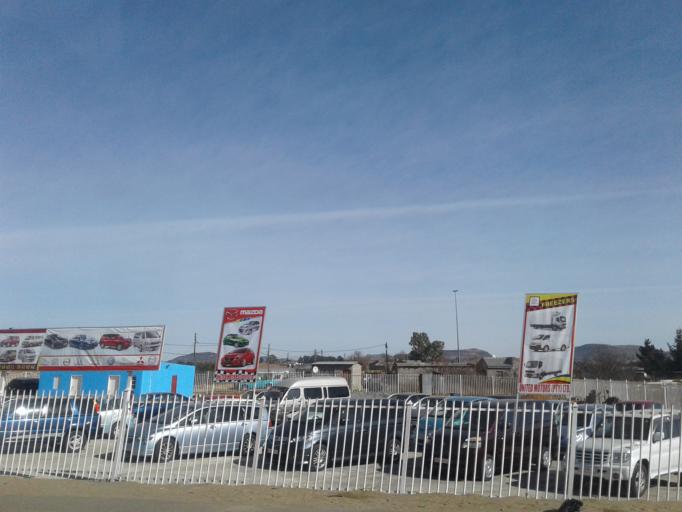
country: LS
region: Maseru
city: Maseru
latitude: -29.2947
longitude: 27.5174
